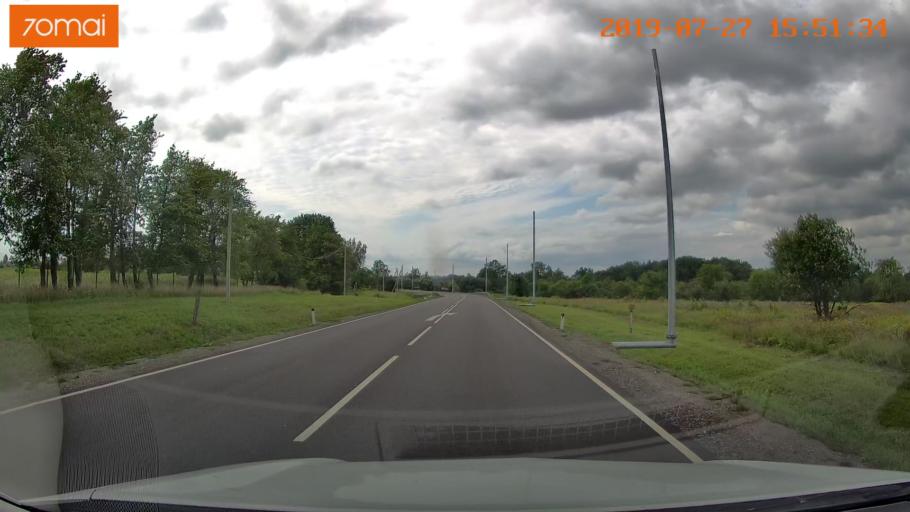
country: RU
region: Kaliningrad
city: Chernyakhovsk
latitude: 54.6028
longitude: 21.9769
